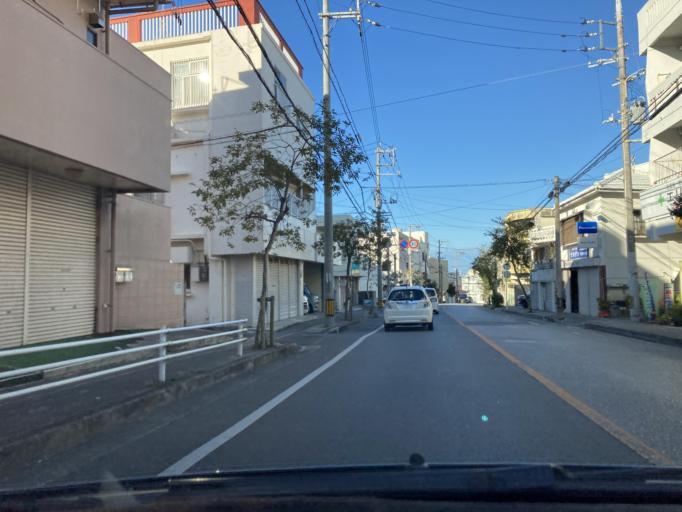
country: JP
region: Okinawa
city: Naha-shi
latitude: 26.2102
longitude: 127.7062
